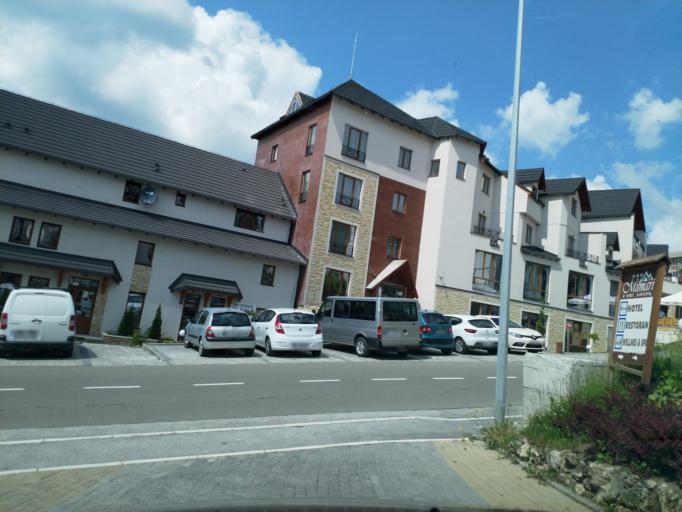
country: RS
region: Central Serbia
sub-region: Raski Okrug
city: Raska
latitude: 43.2756
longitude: 20.7589
